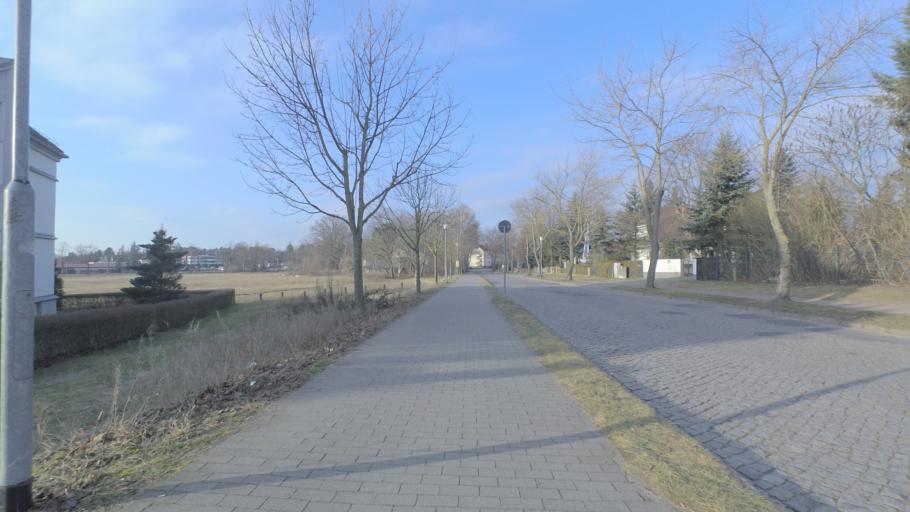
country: DE
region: Brandenburg
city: Rangsdorf
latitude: 52.2918
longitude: 13.4361
